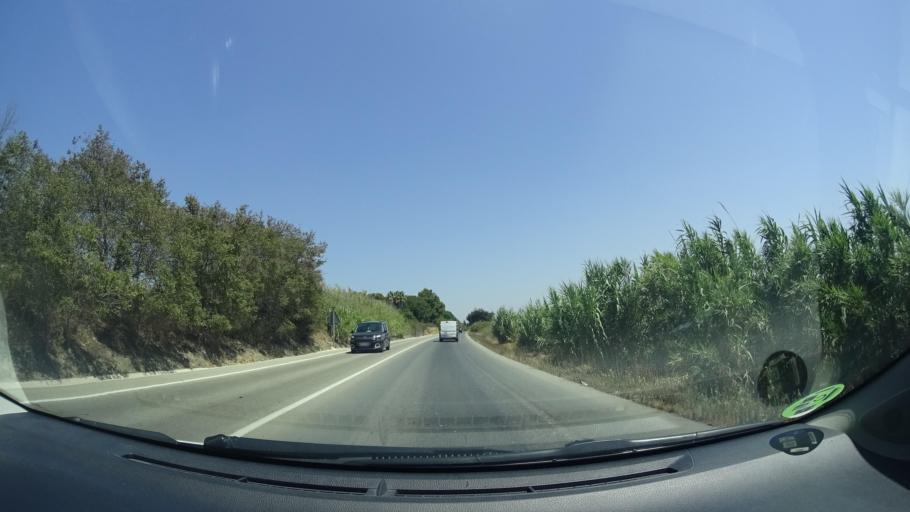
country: ES
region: Andalusia
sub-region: Provincia de Cadiz
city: Jerez de la Frontera
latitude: 36.6581
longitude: -6.0985
